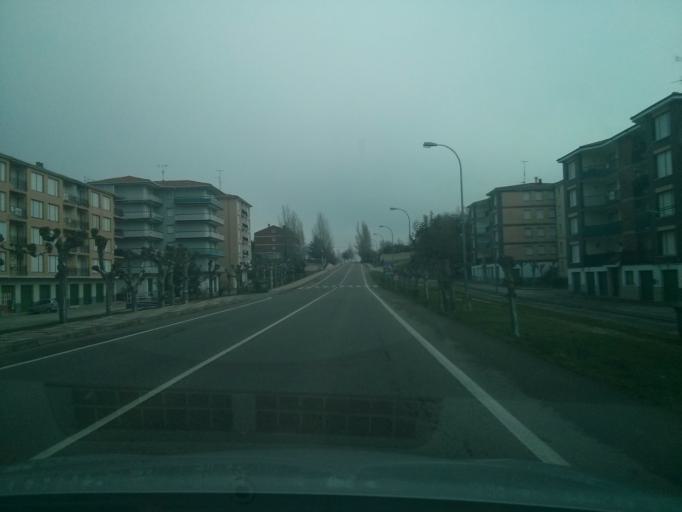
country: ES
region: Castille and Leon
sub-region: Provincia de Burgos
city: Medina de Pomar
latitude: 42.9355
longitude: -3.5107
